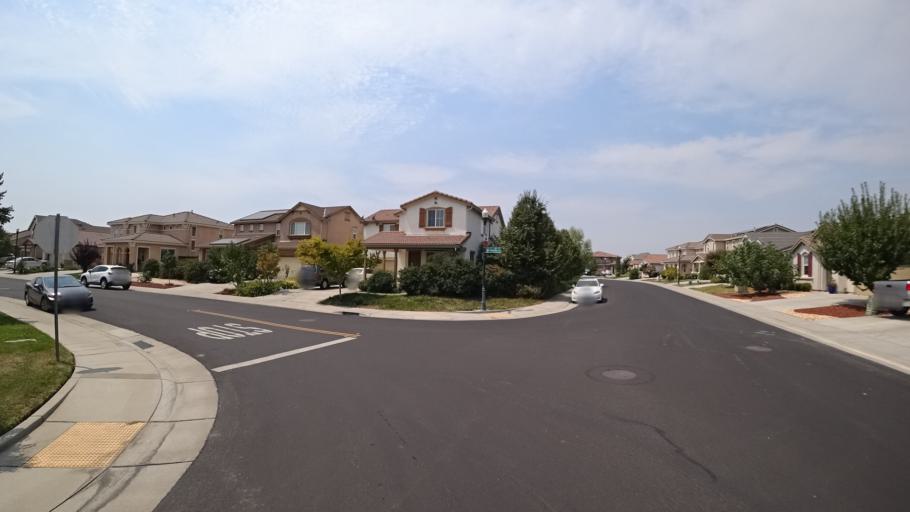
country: US
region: California
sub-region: Sacramento County
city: Laguna
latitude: 38.4040
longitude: -121.4101
